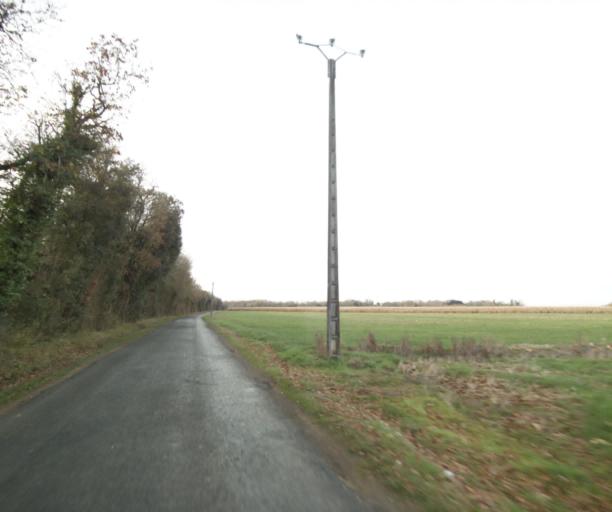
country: FR
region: Poitou-Charentes
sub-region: Departement de la Charente-Maritime
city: Saint-Hilaire-de-Villefranche
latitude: 45.8249
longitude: -0.5740
